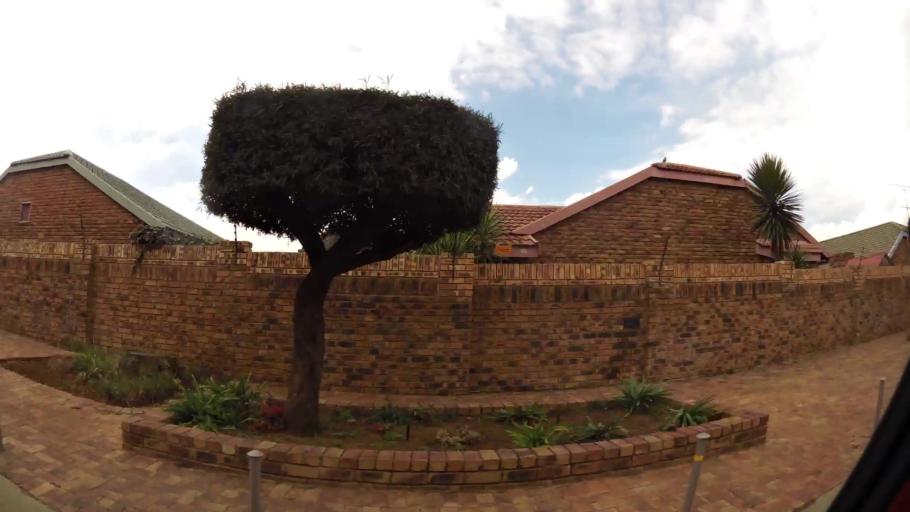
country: ZA
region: Gauteng
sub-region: Sedibeng District Municipality
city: Vanderbijlpark
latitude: -26.7370
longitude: 27.8493
